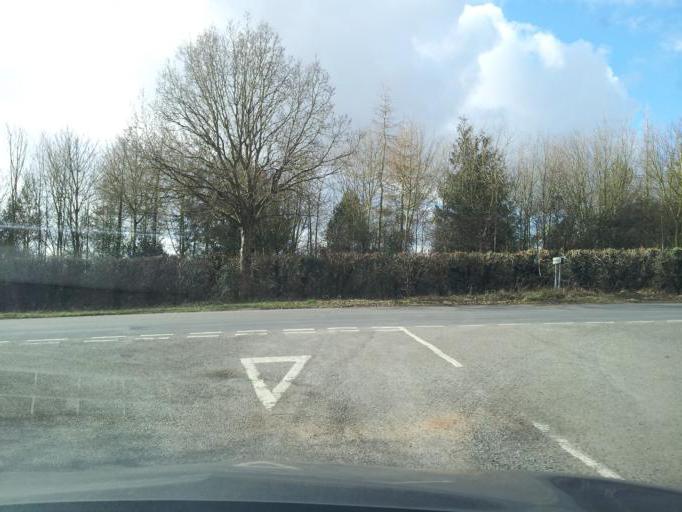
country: GB
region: England
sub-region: Norfolk
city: Mattishall
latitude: 52.6667
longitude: 1.1002
